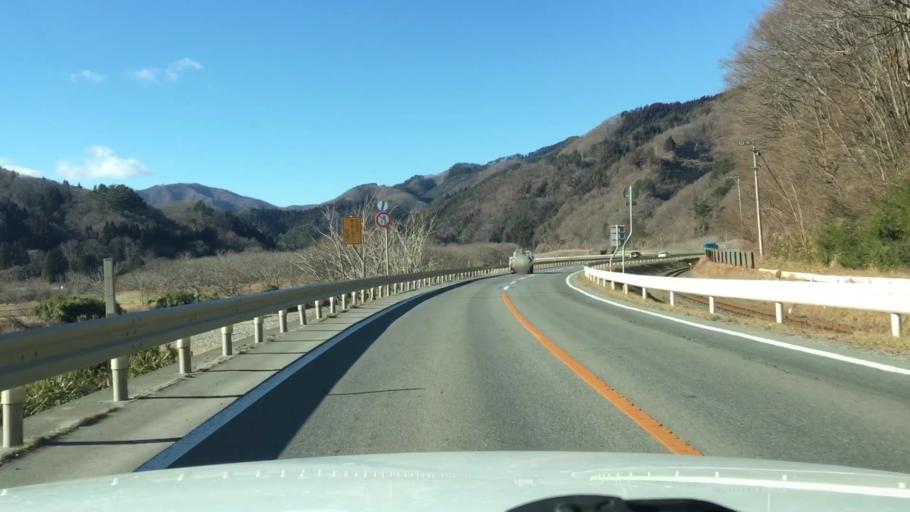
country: JP
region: Iwate
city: Miyako
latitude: 39.6300
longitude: 141.8552
